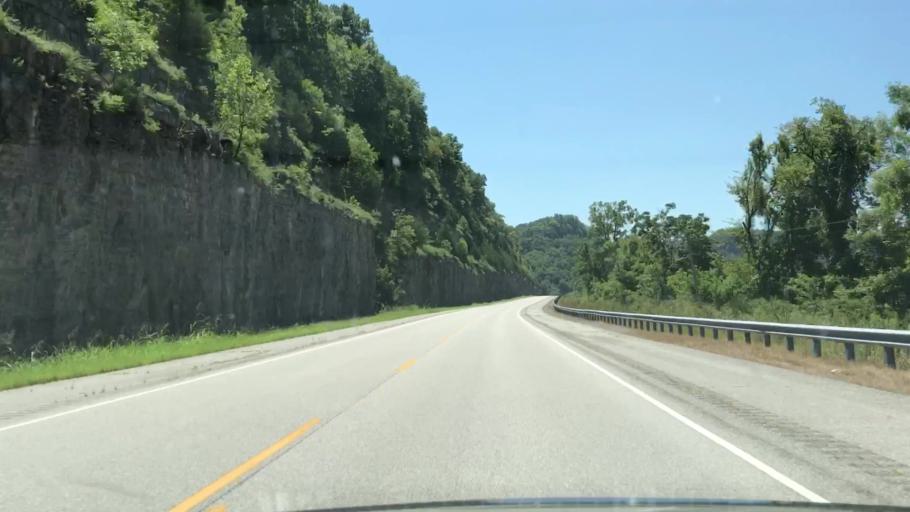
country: US
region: Tennessee
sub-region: Clay County
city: Celina
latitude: 36.4565
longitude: -85.5764
